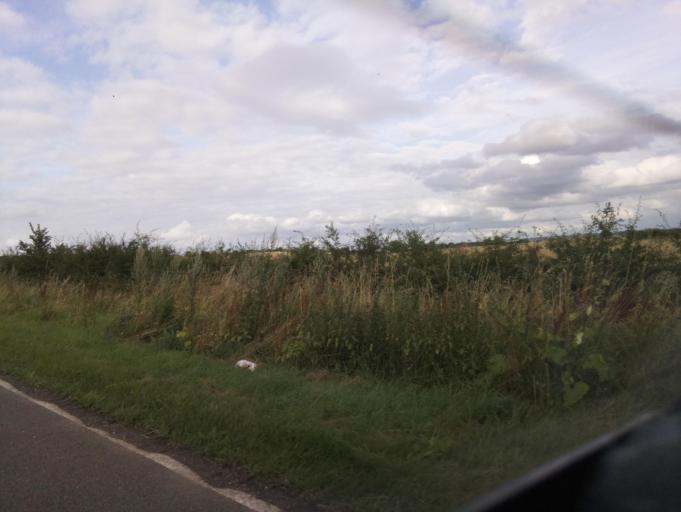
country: GB
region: England
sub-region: Warwickshire
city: Dunchurch
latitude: 52.3250
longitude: -1.3023
